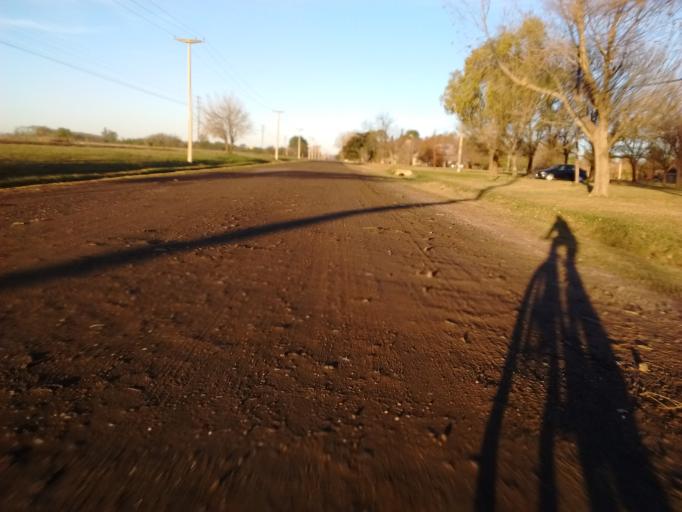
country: AR
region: Santa Fe
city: Funes
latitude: -32.9130
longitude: -60.8346
